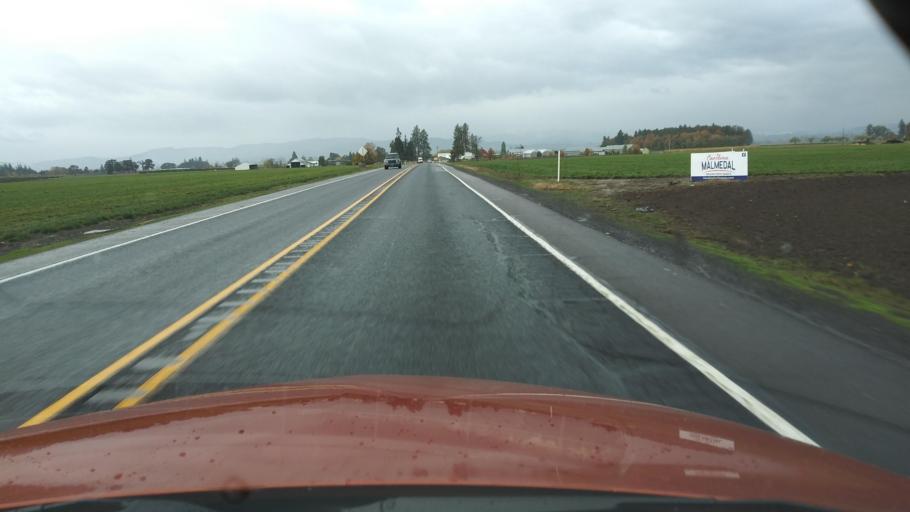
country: US
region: Oregon
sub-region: Washington County
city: North Plains
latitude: 45.5741
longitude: -123.0253
